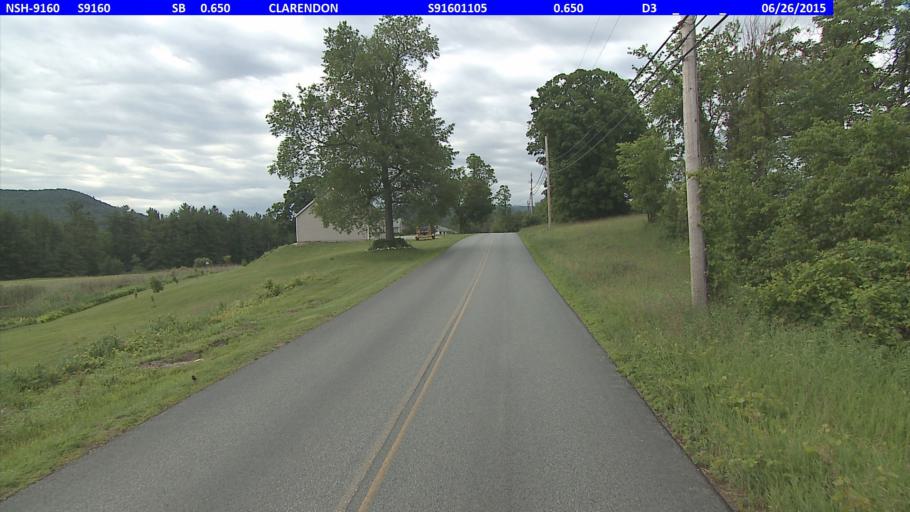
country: US
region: Vermont
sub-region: Rutland County
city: Rutland
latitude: 43.5368
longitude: -72.9471
